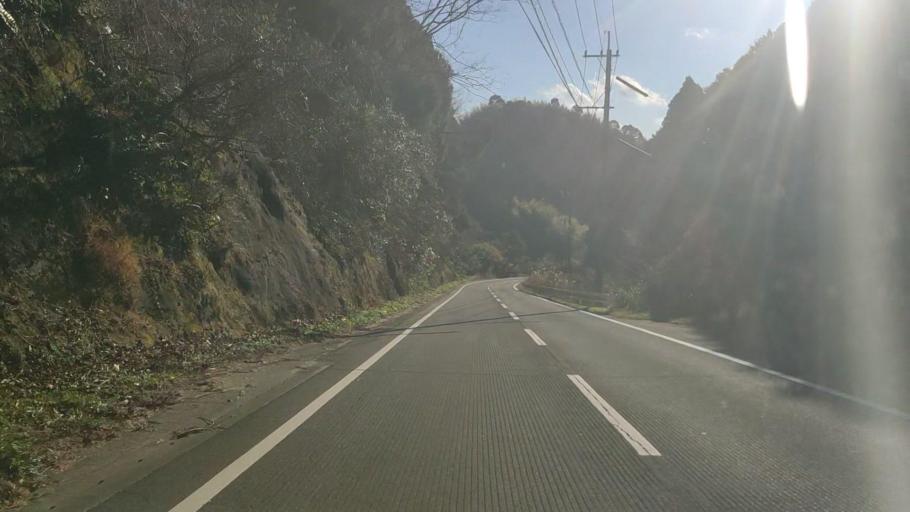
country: JP
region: Saga Prefecture
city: Kanzakimachi-kanzaki
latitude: 33.3947
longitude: 130.2712
